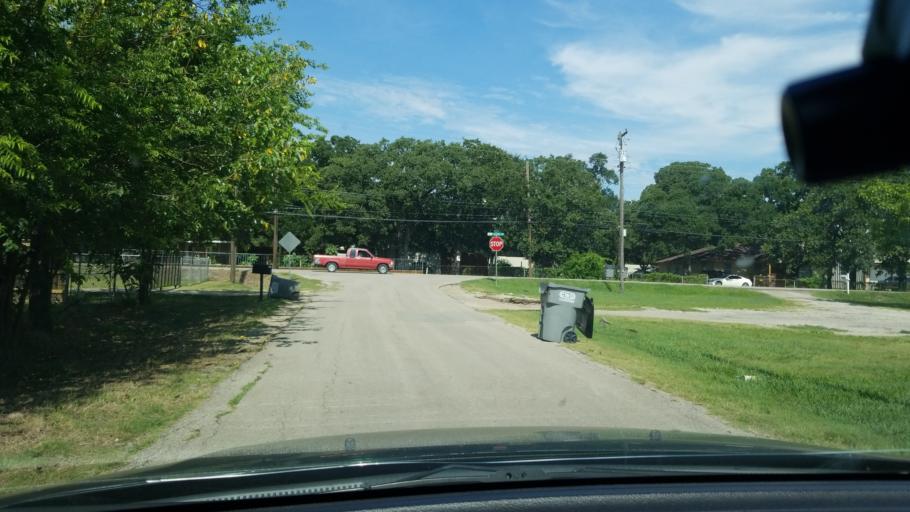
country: US
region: Texas
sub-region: Dallas County
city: Balch Springs
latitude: 32.7278
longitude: -96.6307
